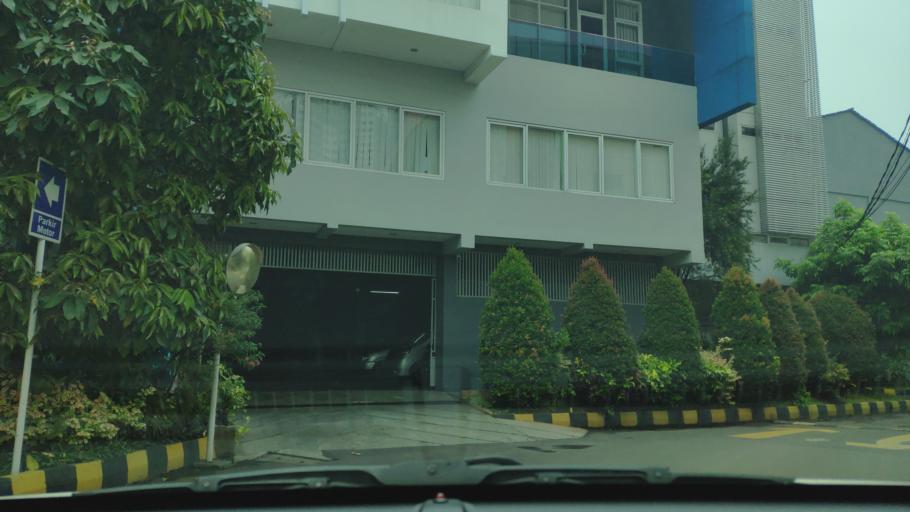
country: ID
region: Jakarta Raya
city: Jakarta
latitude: -6.1657
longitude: 106.8185
